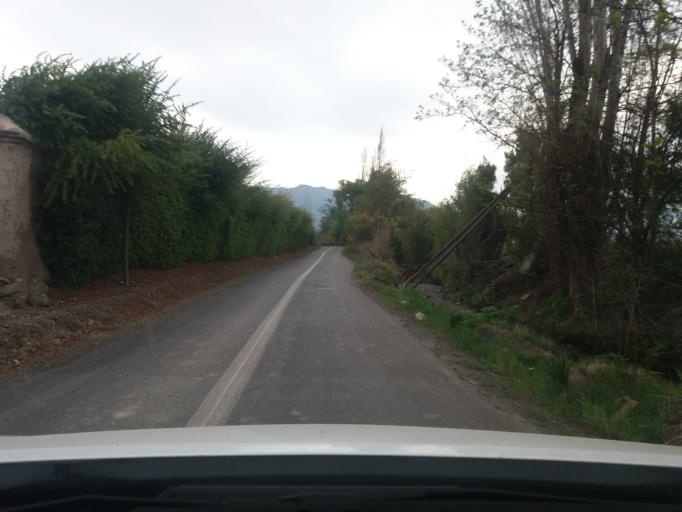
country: CL
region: Valparaiso
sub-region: Provincia de Los Andes
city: Los Andes
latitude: -32.8557
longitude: -70.6511
